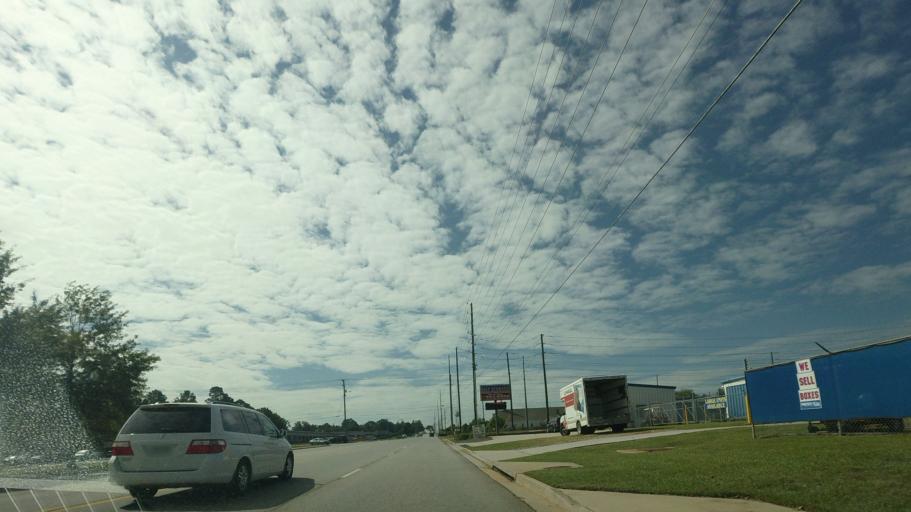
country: US
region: Georgia
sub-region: Houston County
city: Centerville
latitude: 32.6326
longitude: -83.6898
